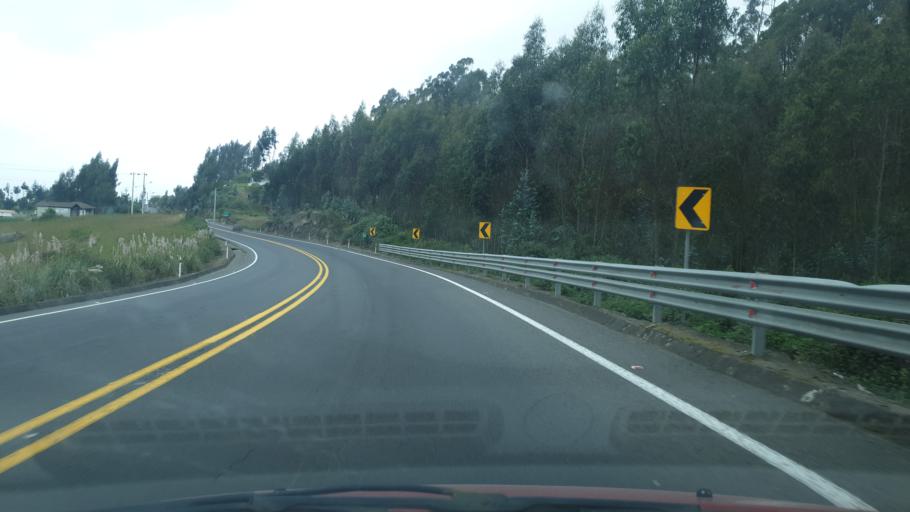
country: EC
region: Tungurahua
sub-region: Canton Quero
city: Quero
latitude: -1.3786
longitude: -78.6500
